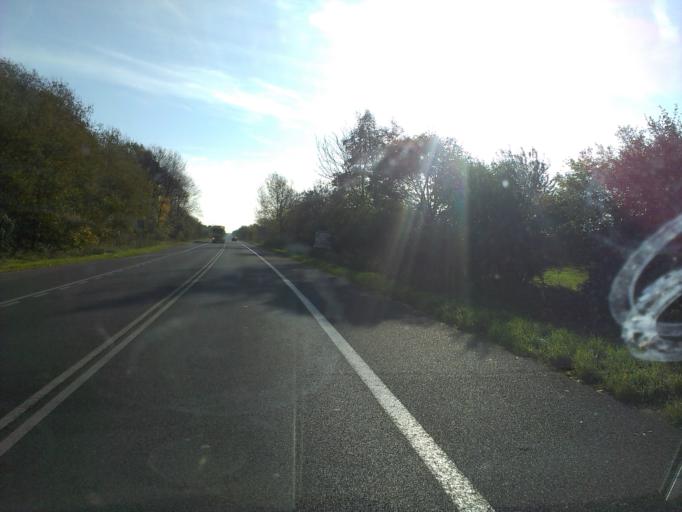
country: PL
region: West Pomeranian Voivodeship
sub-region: Powiat pyrzycki
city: Pyrzyce
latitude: 53.1677
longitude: 14.8593
